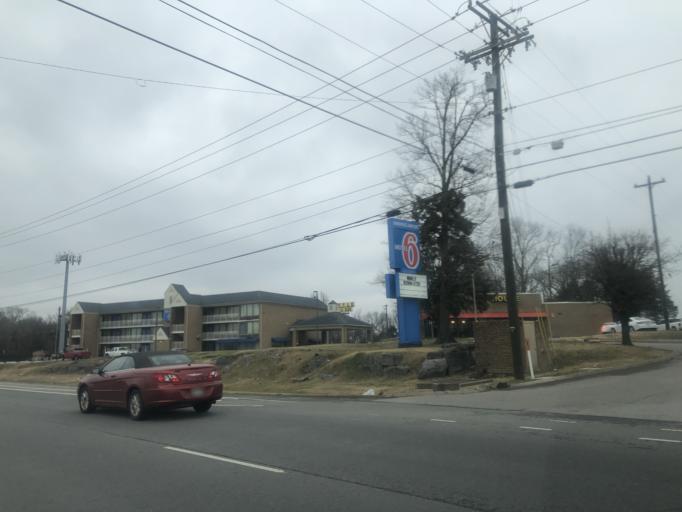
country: US
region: Tennessee
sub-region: Davidson County
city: Lakewood
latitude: 36.1539
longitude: -86.6256
